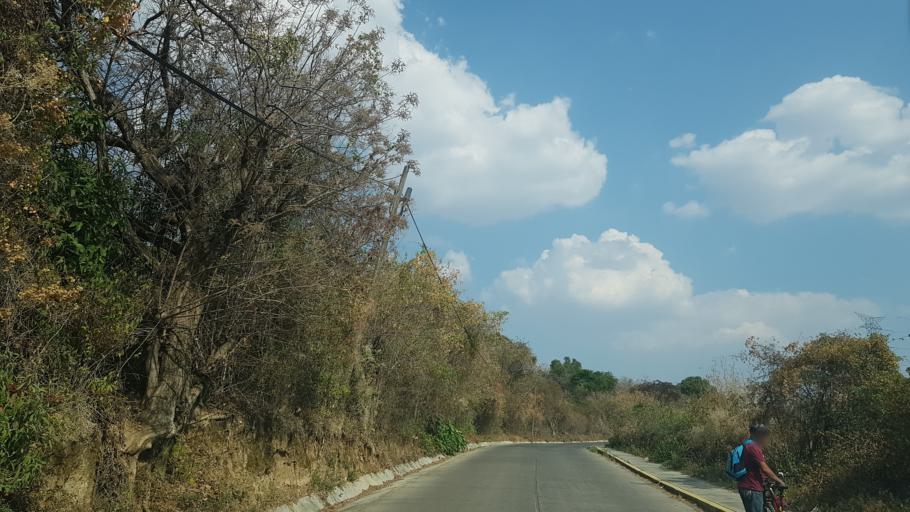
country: MX
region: Puebla
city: San Juan Amecac
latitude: 18.8298
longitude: -98.7048
